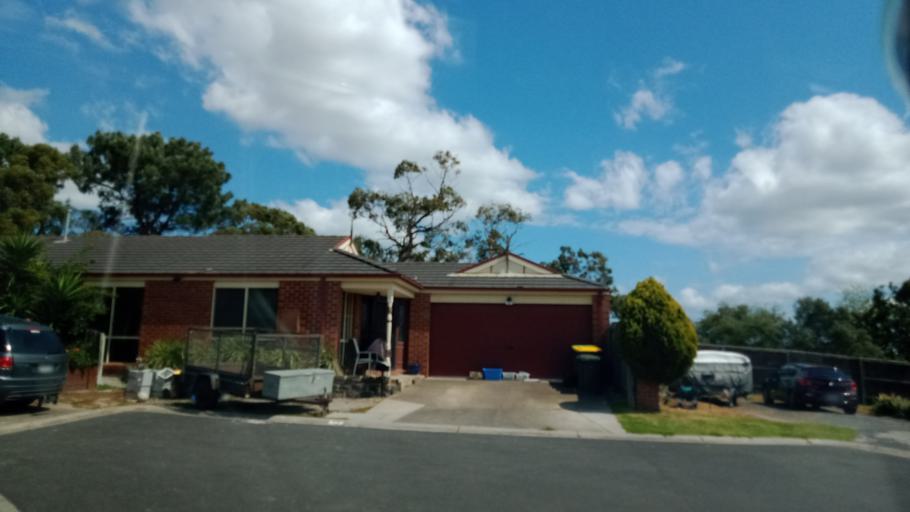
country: AU
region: Victoria
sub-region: Frankston
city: Carrum Downs
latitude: -38.0955
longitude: 145.1916
